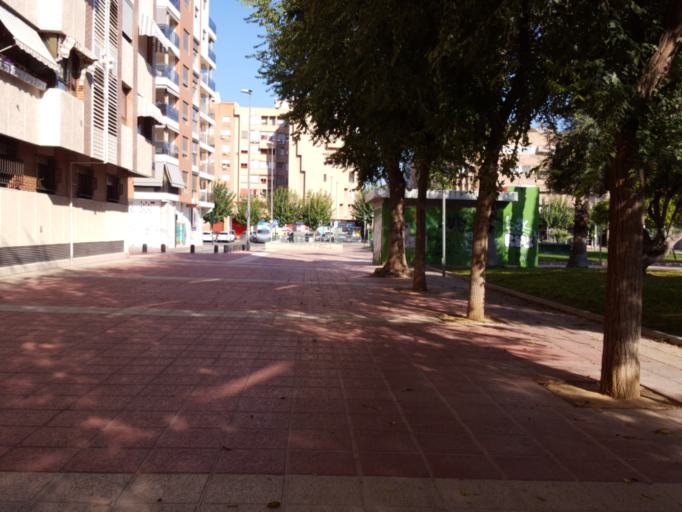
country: ES
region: Murcia
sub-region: Murcia
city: Murcia
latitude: 37.9960
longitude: -1.1319
